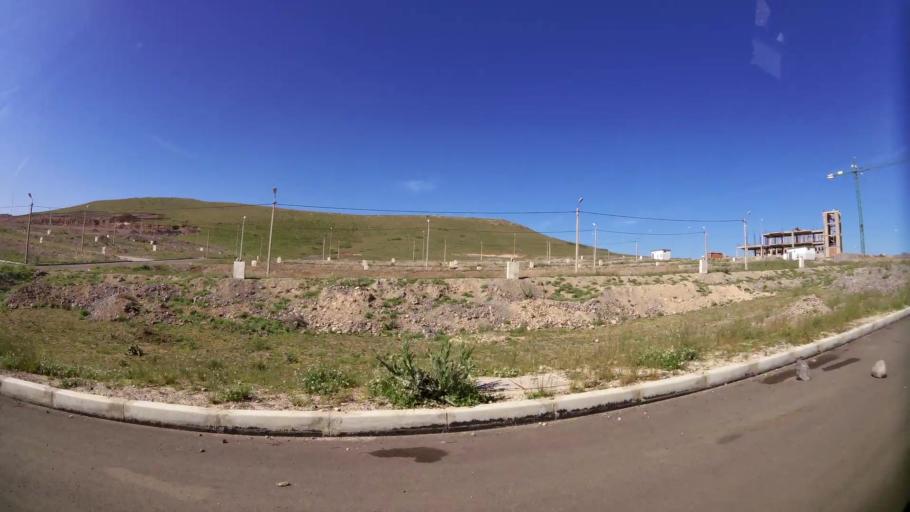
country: MA
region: Oriental
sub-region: Oujda-Angad
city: Oujda
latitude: 34.6491
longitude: -1.9567
